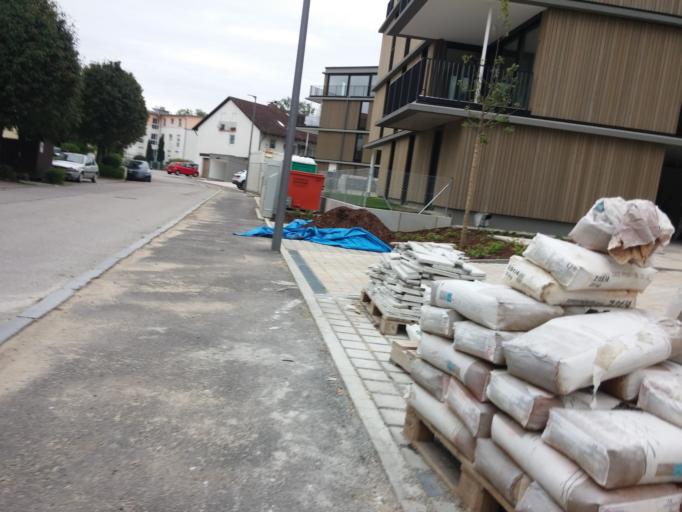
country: DE
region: Bavaria
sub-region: Upper Bavaria
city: Pfaffenhofen an der Ilm
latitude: 48.5316
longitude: 11.5137
